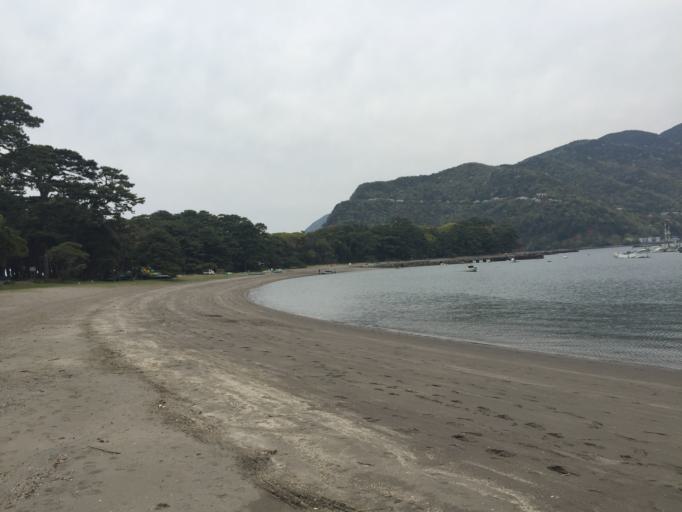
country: JP
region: Shizuoka
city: Heda
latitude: 34.9732
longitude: 138.7641
